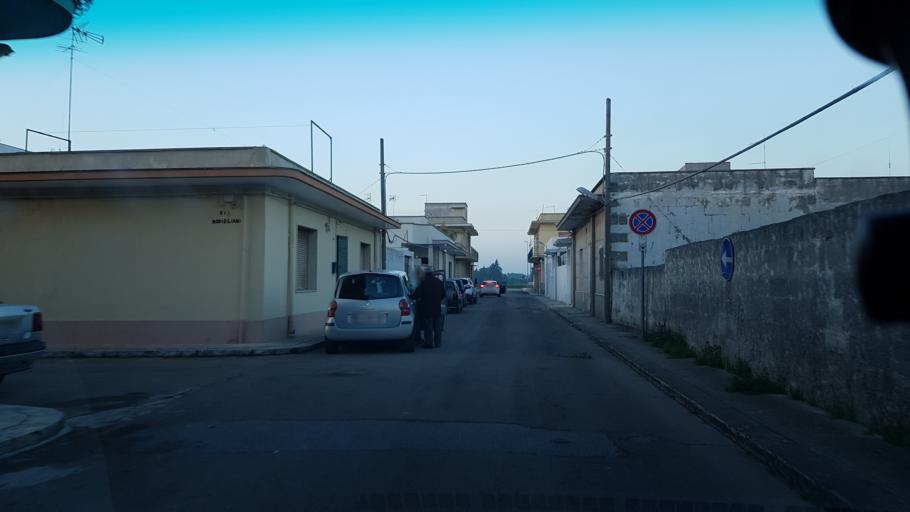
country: IT
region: Apulia
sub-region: Provincia di Brindisi
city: Mesagne
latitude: 40.5623
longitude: 17.7950
